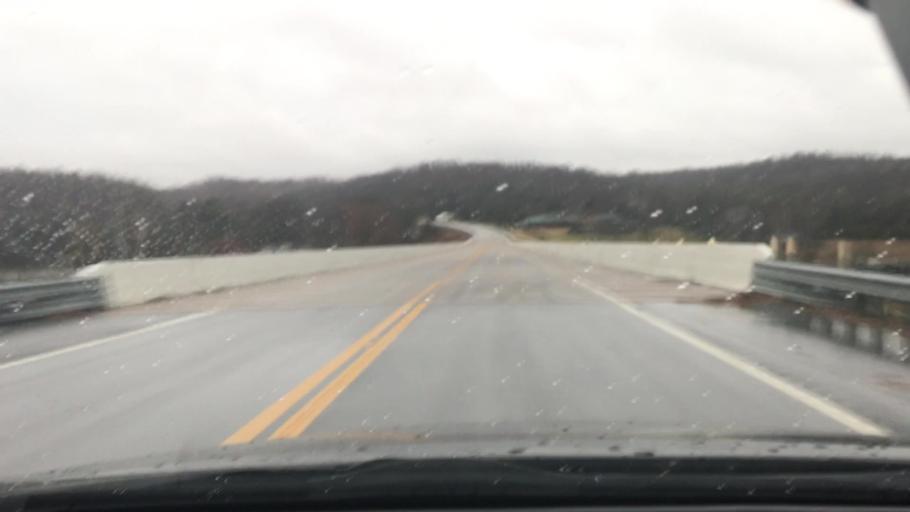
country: US
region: Tennessee
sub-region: Cheatham County
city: Ashland City
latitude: 36.2860
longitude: -87.1467
